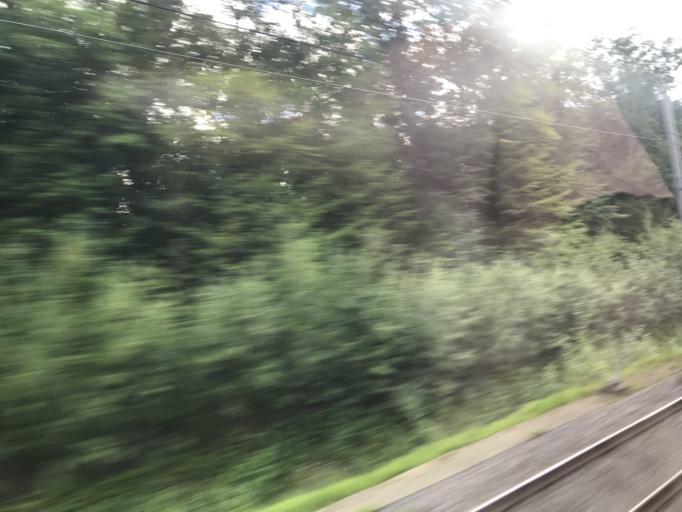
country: LU
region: Luxembourg
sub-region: Canton de Capellen
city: Bascharage
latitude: 49.5548
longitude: 5.9072
